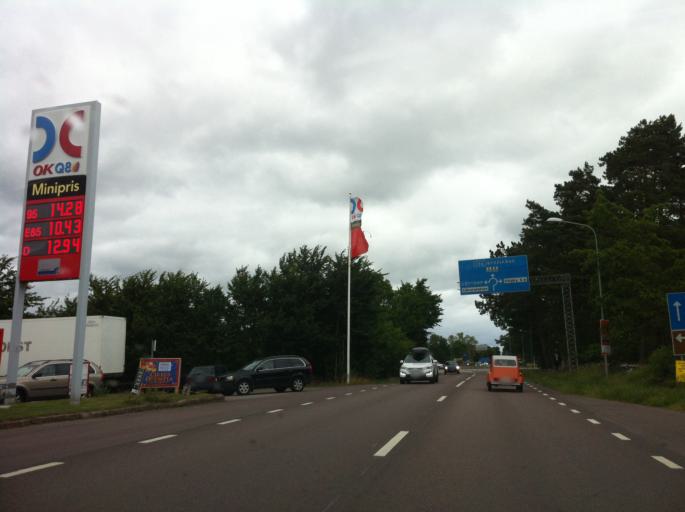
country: SE
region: Kalmar
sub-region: Borgholms Kommun
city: Borgholm
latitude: 57.1634
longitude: 17.0126
